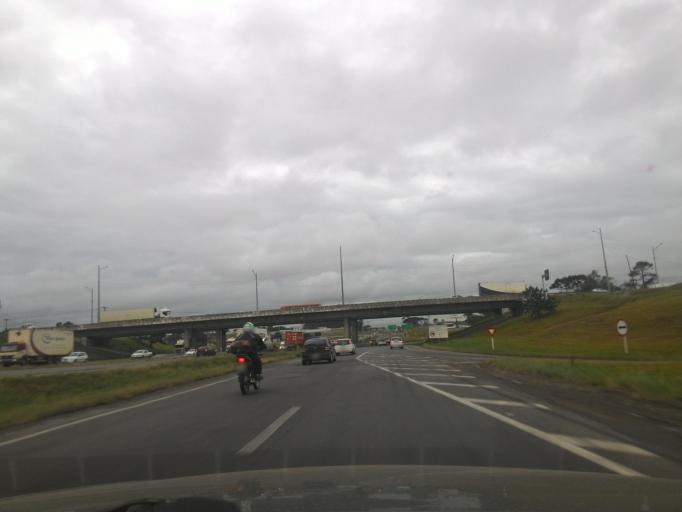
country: BR
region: Parana
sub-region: Sao Jose Dos Pinhais
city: Sao Jose dos Pinhais
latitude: -25.5444
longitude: -49.3049
